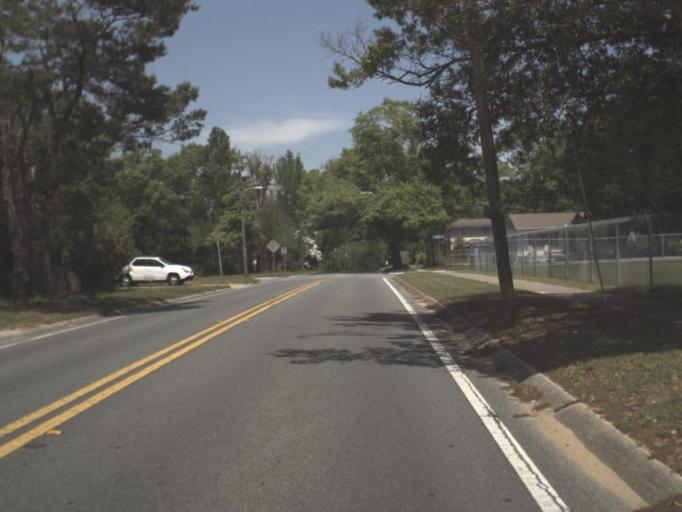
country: US
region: Florida
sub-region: Escambia County
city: East Pensacola Heights
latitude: 30.4287
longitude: -87.1832
